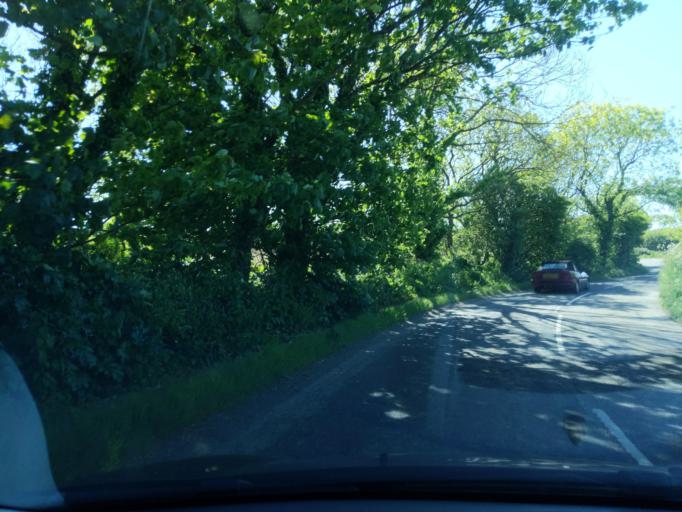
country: GB
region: England
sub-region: Cornwall
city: St. Buryan
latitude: 50.0839
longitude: -5.6065
